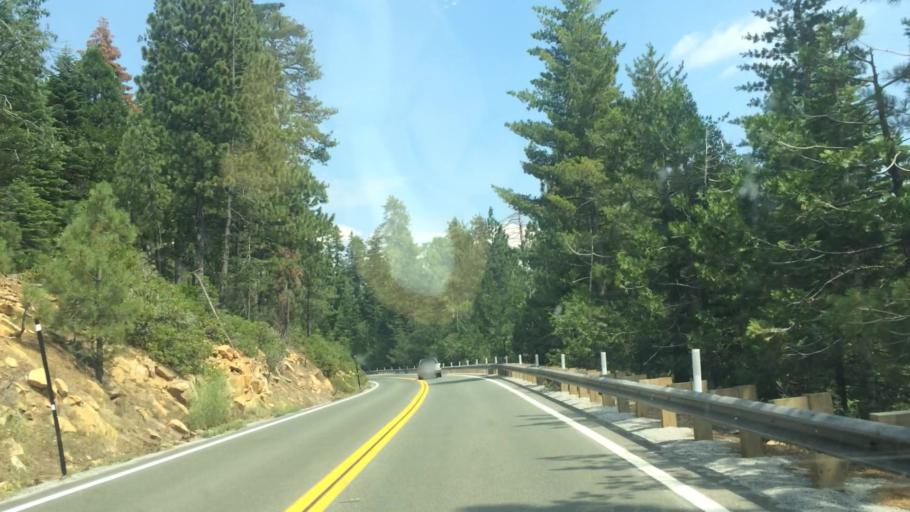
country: US
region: California
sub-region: Amador County
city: Pioneer
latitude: 38.5443
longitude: -120.3289
